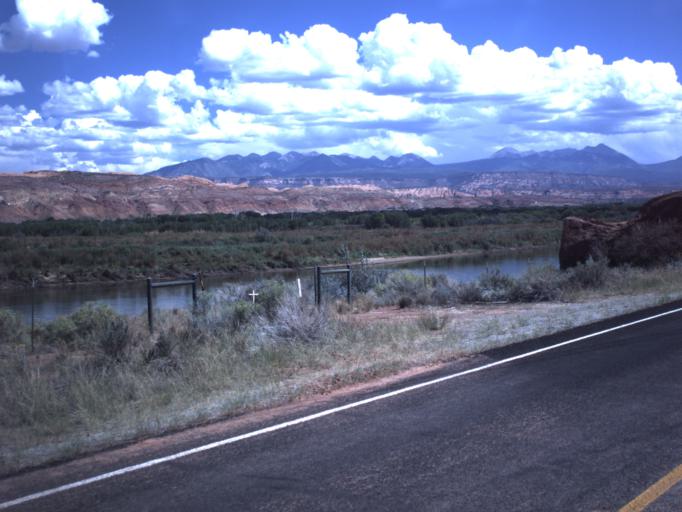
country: US
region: Utah
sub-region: Grand County
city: Moab
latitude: 38.5837
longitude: -109.5895
